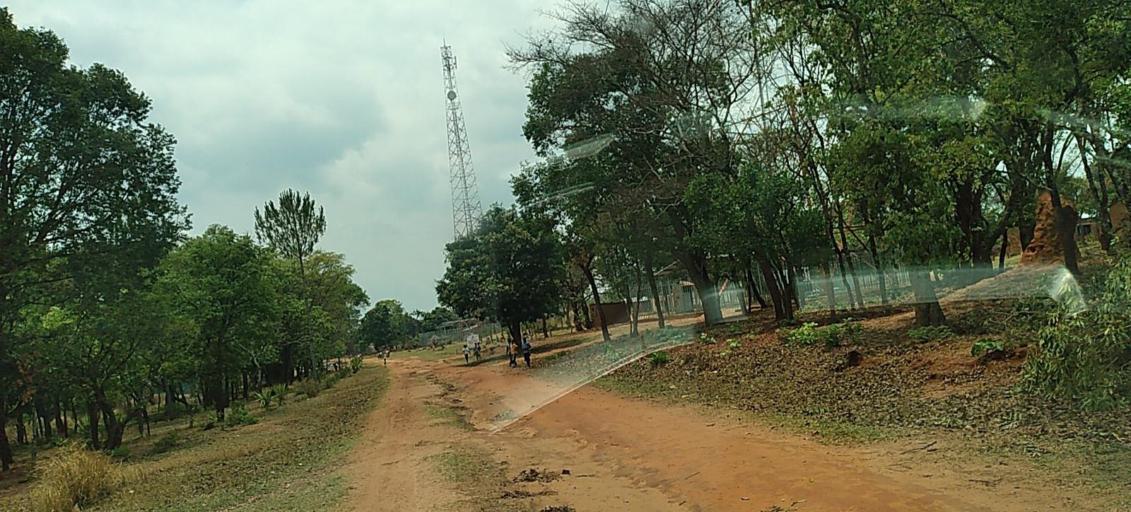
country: ZM
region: North-Western
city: Mwinilunga
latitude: -11.5212
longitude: 24.7887
